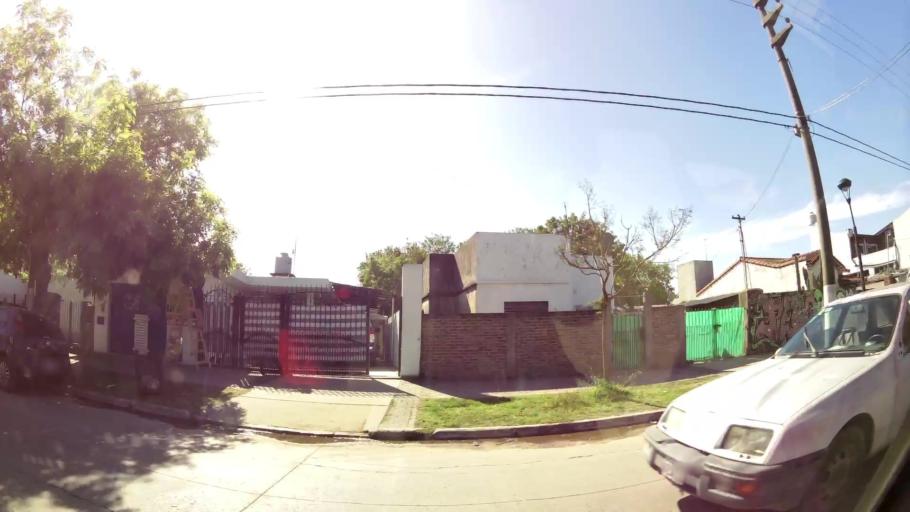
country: AR
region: Buenos Aires
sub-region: Partido de Quilmes
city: Quilmes
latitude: -34.8046
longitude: -58.2232
